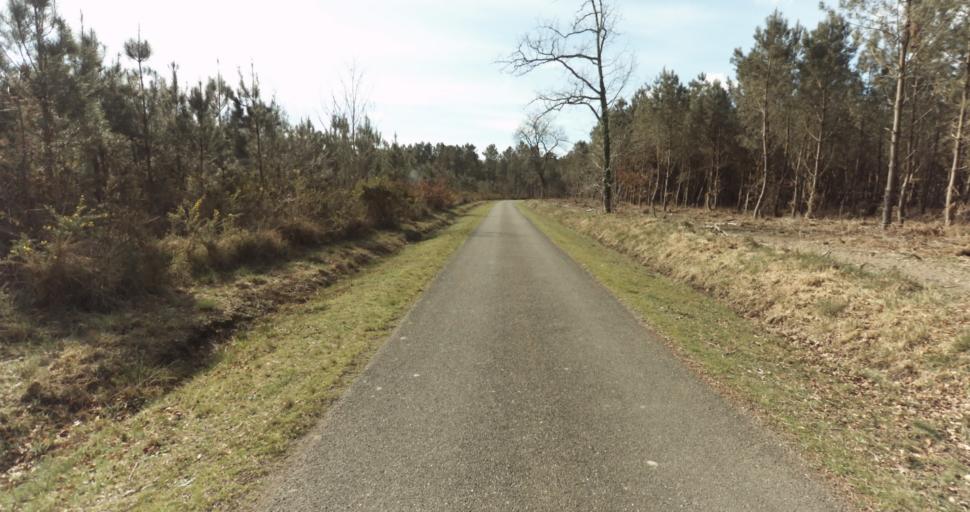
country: FR
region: Aquitaine
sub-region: Departement des Landes
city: Roquefort
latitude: 44.0694
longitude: -0.3313
